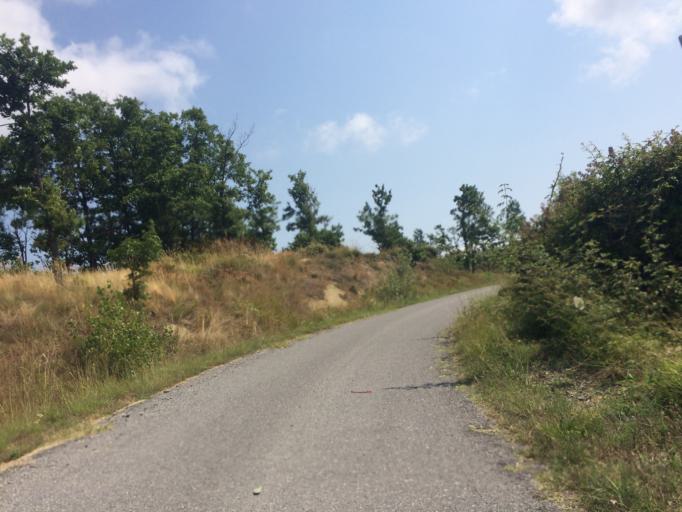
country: IT
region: Piedmont
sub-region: Provincia di Alessandria
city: Pareto
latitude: 44.5015
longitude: 8.3699
